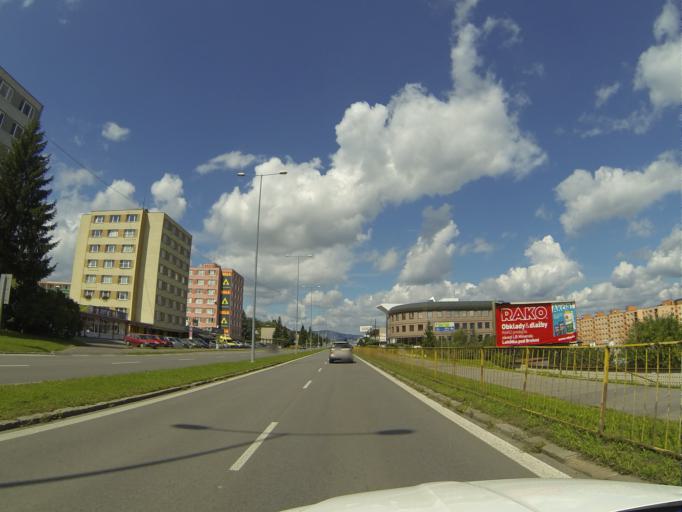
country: SK
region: Banskobystricky
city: Ziar nad Hronom
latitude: 48.5915
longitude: 18.8539
